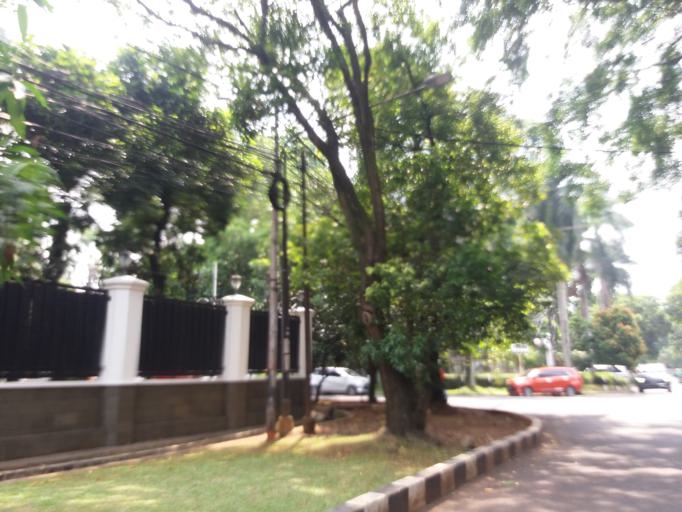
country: ID
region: Jakarta Raya
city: Jakarta
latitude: -6.2314
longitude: 106.8032
